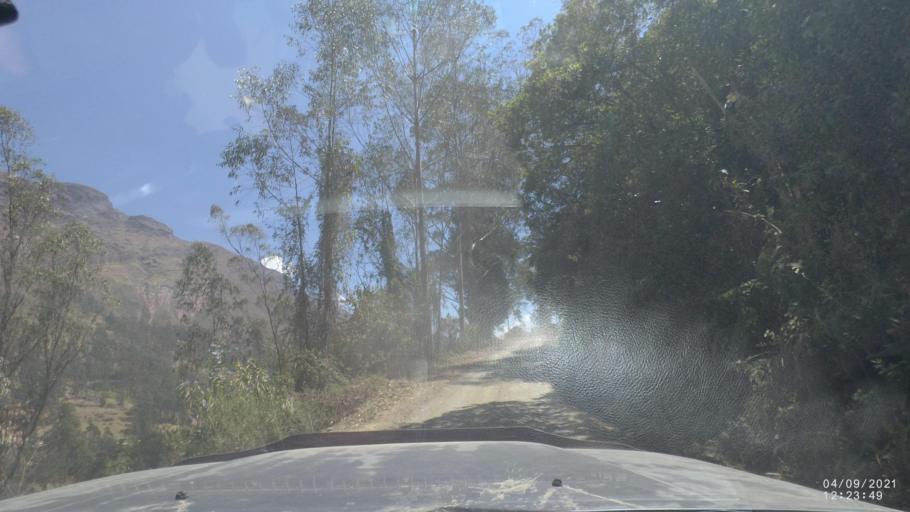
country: BO
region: Cochabamba
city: Colchani
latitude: -17.2373
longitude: -66.5255
